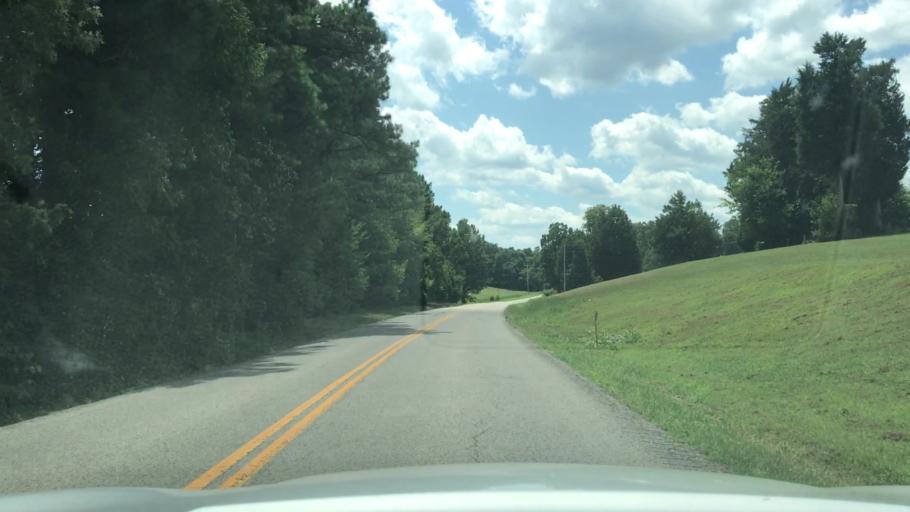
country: US
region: Kentucky
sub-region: Muhlenberg County
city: Greenville
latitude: 37.1393
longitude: -87.2646
